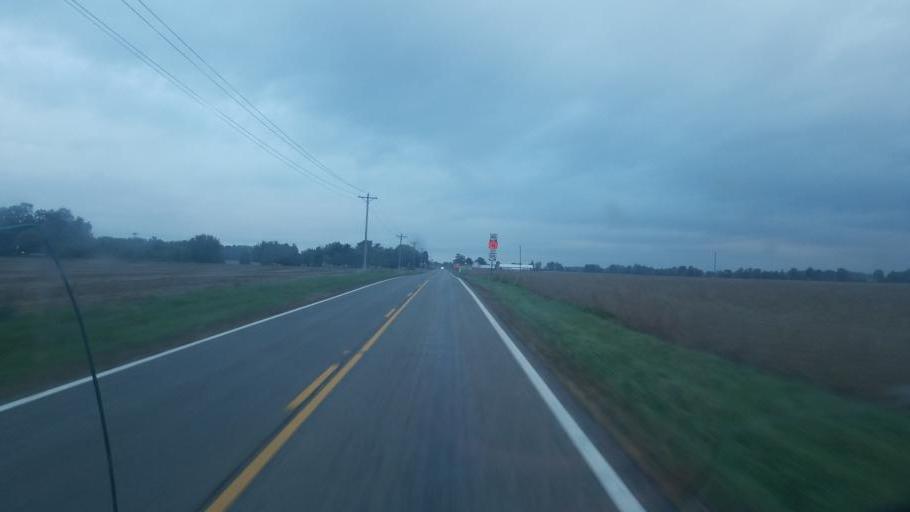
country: US
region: Ohio
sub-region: Morrow County
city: Cardington
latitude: 40.5839
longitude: -82.9622
